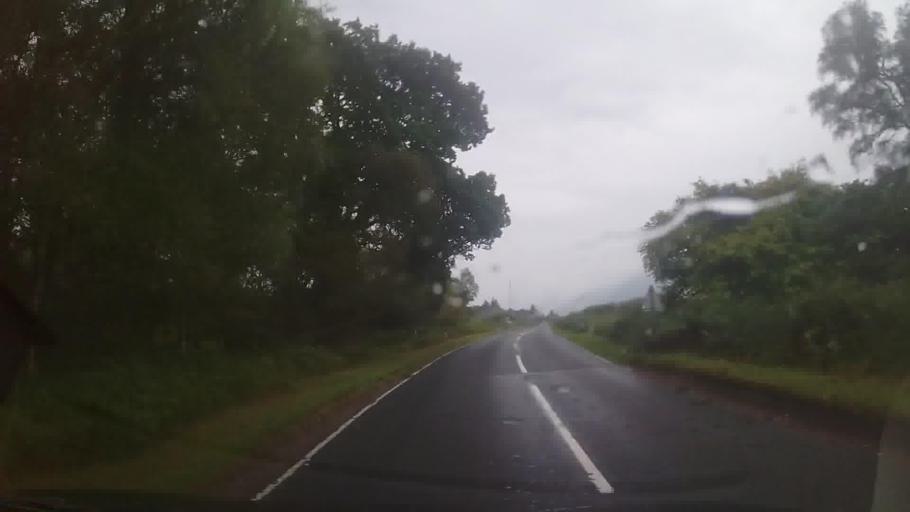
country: GB
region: Scotland
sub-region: Highland
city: Fort William
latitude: 56.7135
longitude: -5.2959
